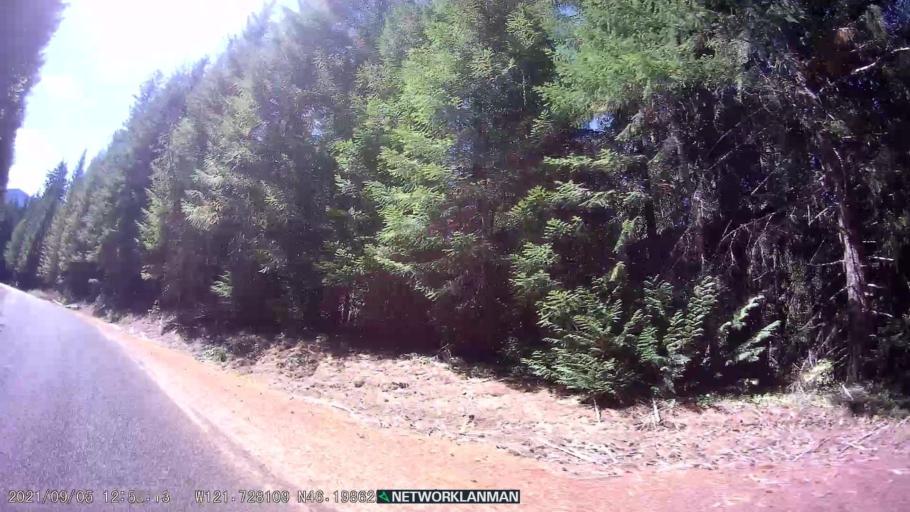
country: US
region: Washington
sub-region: Skamania County
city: Carson
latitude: 46.1985
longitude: -121.7284
